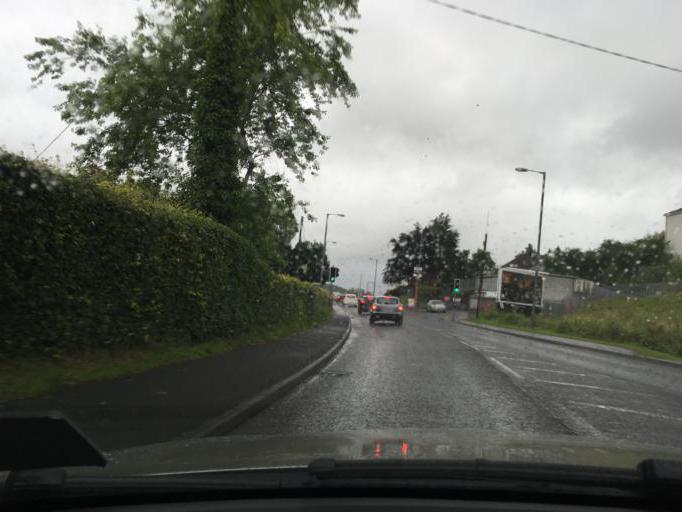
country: GB
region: Northern Ireland
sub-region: Fermanagh District
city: Enniskillen
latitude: 54.3526
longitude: -7.6365
